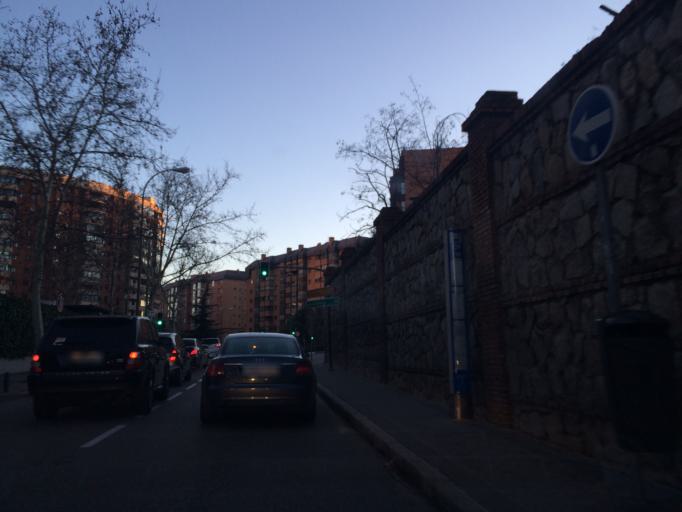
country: ES
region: Madrid
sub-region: Provincia de Madrid
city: Pinar de Chamartin
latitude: 40.4741
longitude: -3.6774
